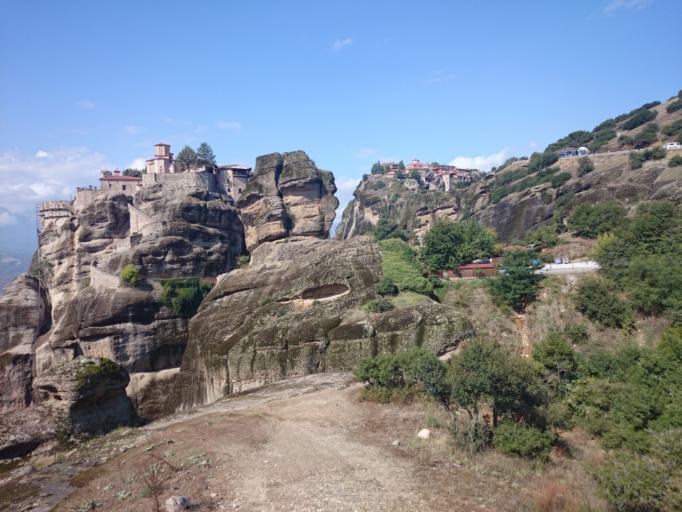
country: GR
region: Thessaly
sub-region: Trikala
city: Kastraki
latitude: 39.7256
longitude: 21.6322
